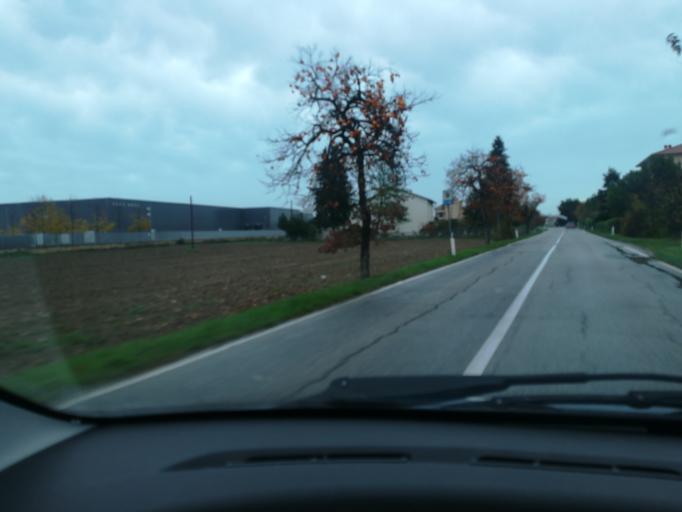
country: IT
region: The Marches
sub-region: Provincia di Macerata
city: Borgo Stazione
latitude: 43.2785
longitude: 13.6200
